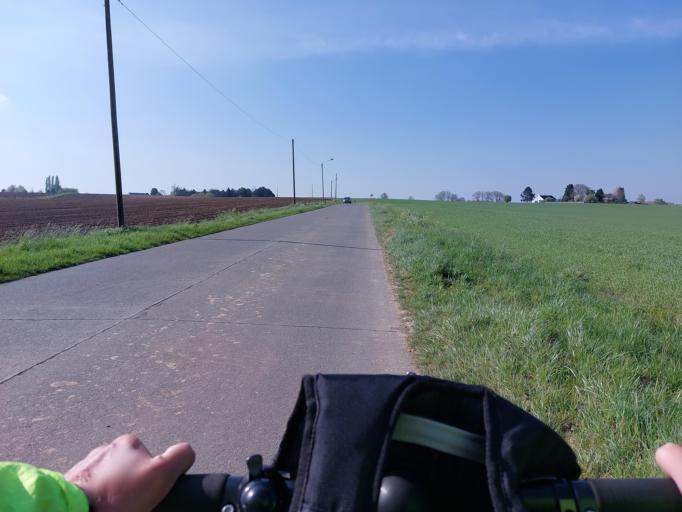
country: BE
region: Wallonia
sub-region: Province du Hainaut
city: Ecaussinnes-d'Enghien
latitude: 50.5351
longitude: 4.1470
